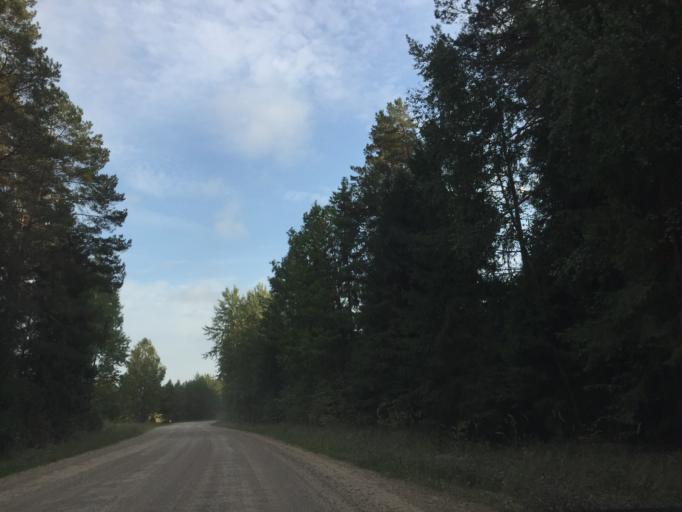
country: LV
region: Baldone
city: Baldone
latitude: 56.7941
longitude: 24.4383
